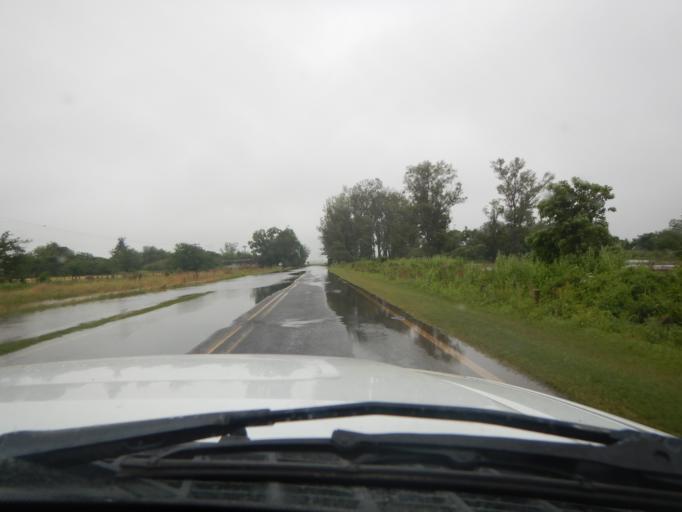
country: AR
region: Santa Fe
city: Recreo
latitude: -31.3928
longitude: -60.7473
